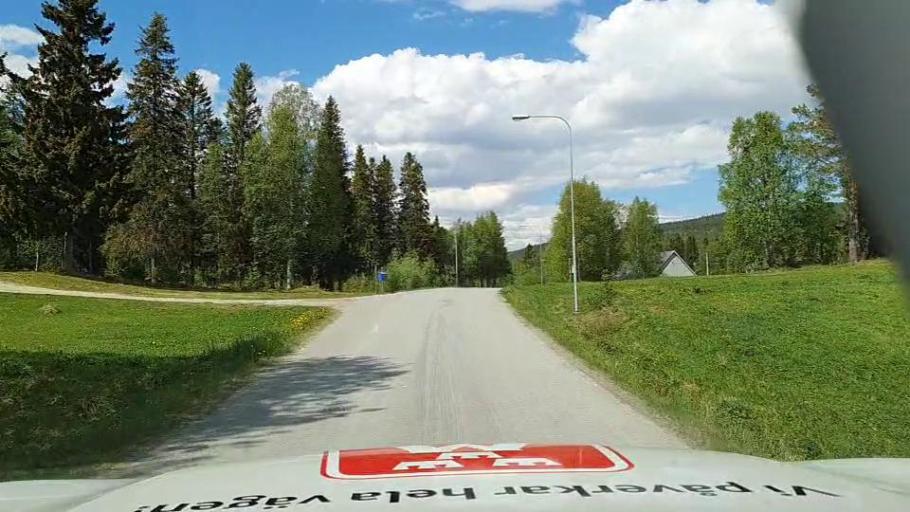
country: NO
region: Nord-Trondelag
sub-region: Lierne
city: Sandvika
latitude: 64.1200
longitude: 14.1412
